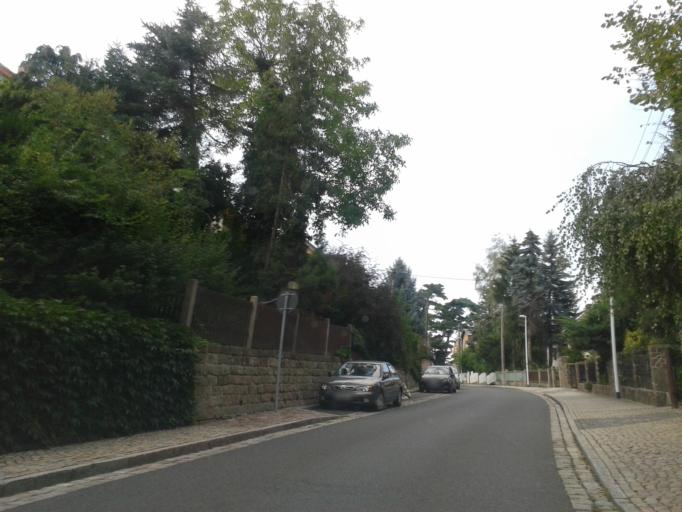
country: DE
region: Saxony
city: Radebeul
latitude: 51.0834
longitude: 13.6248
